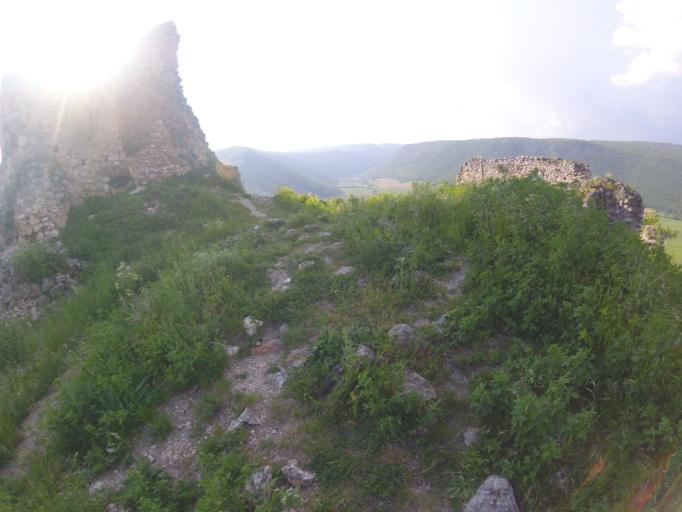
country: SK
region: Kosicky
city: Medzev
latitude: 48.6110
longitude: 20.8745
